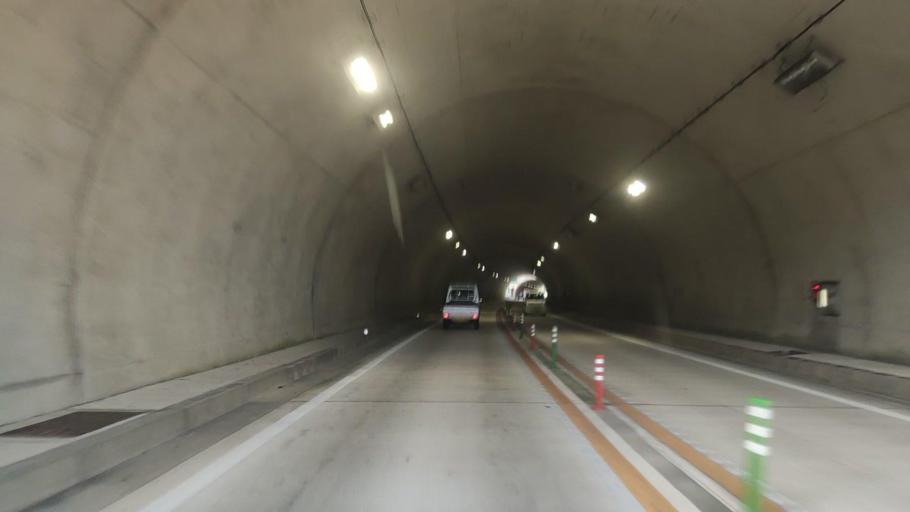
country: JP
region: Wakayama
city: Tanabe
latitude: 33.6404
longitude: 135.4095
